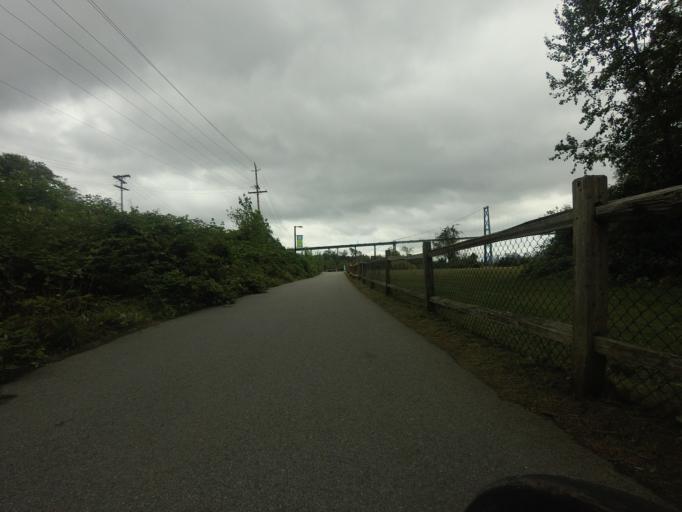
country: CA
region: British Columbia
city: West End
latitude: 49.3221
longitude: -123.1411
